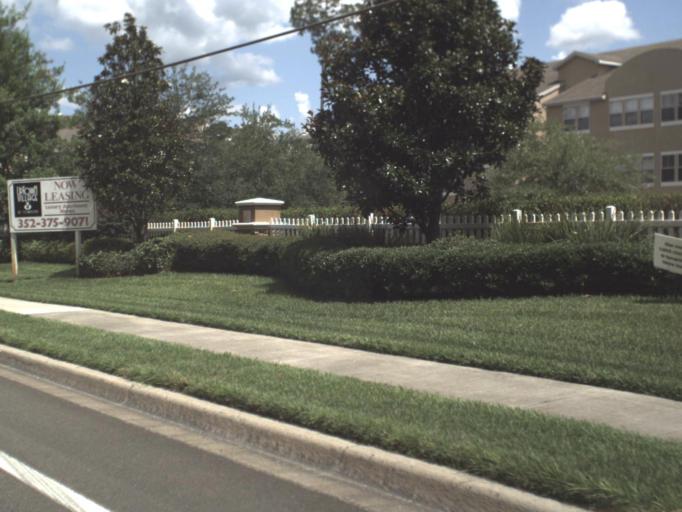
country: US
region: Florida
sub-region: Alachua County
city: Gainesville
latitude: 29.6884
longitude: -82.3577
